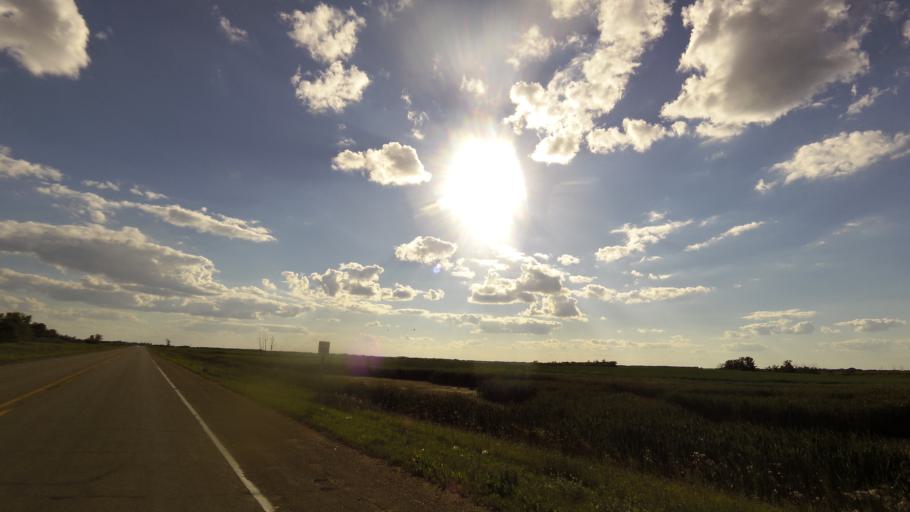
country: CA
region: Saskatchewan
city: Lanigan
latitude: 51.8734
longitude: -105.1955
